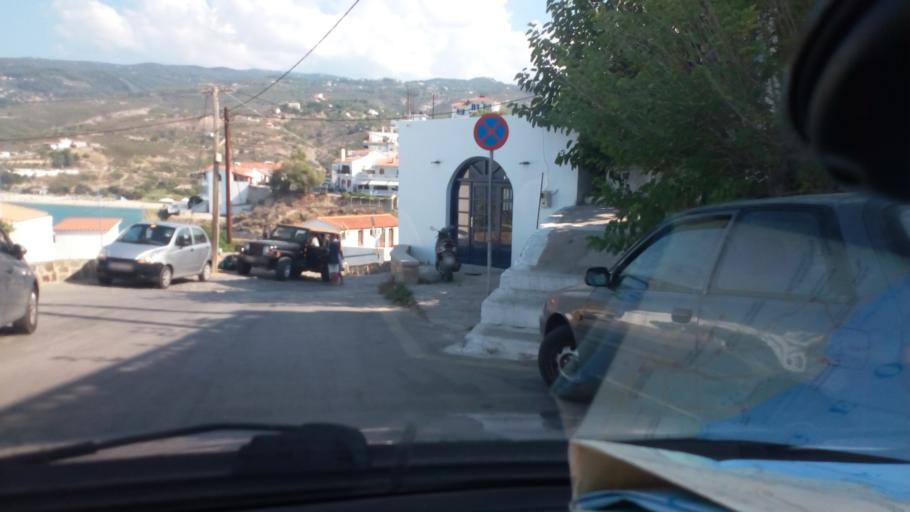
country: GR
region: North Aegean
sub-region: Nomos Samou
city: Agios Kirykos
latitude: 37.6343
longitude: 26.0876
